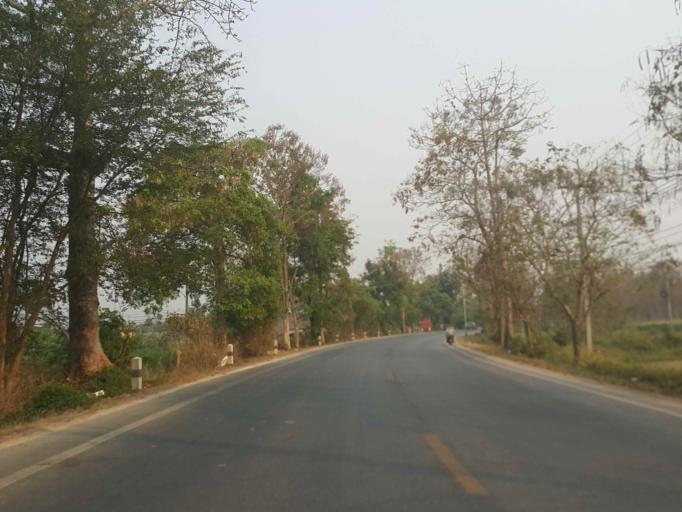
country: TH
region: Chiang Mai
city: Mae Taeng
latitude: 18.9994
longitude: 98.9757
